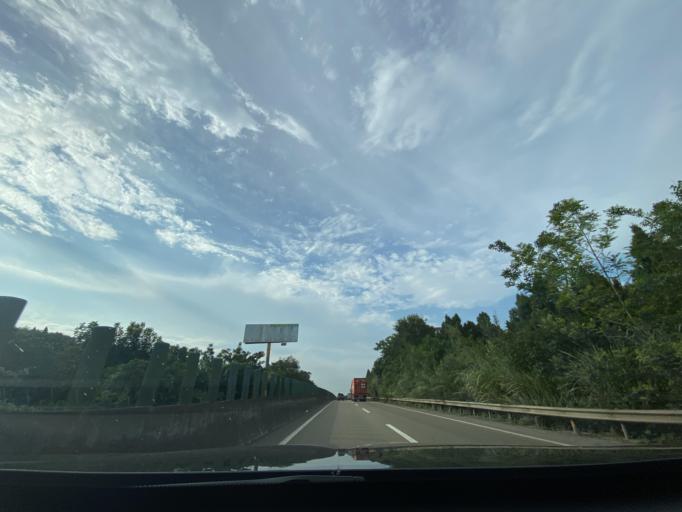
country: CN
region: Sichuan
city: Yanjiang
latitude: 30.0496
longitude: 104.5985
